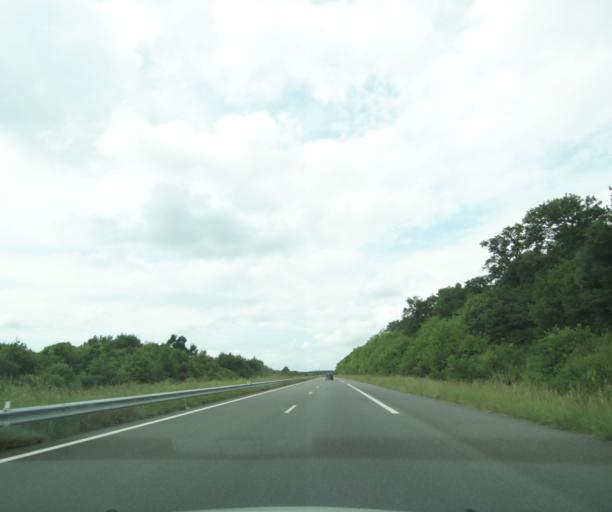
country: FR
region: Centre
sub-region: Departement du Cher
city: Orval
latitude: 46.7978
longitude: 2.4136
